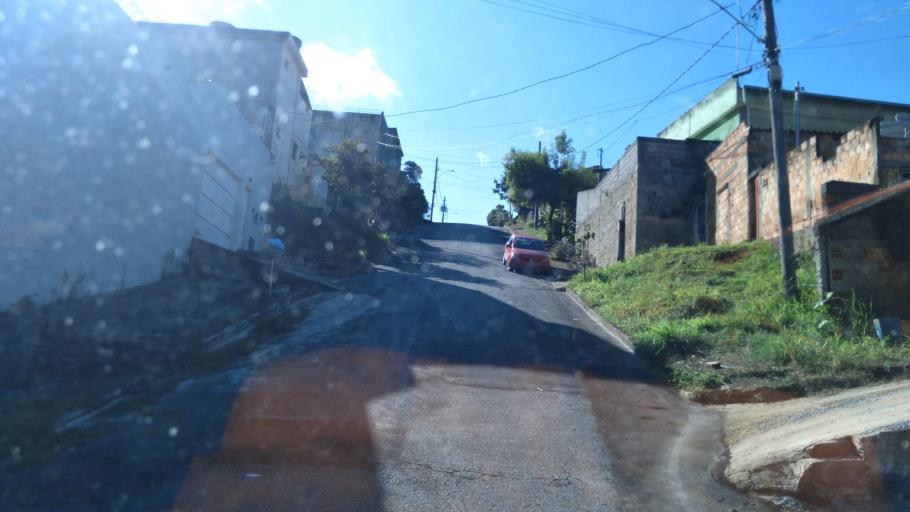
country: BR
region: Minas Gerais
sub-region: Santa Luzia
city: Santa Luzia
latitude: -19.8279
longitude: -43.9019
